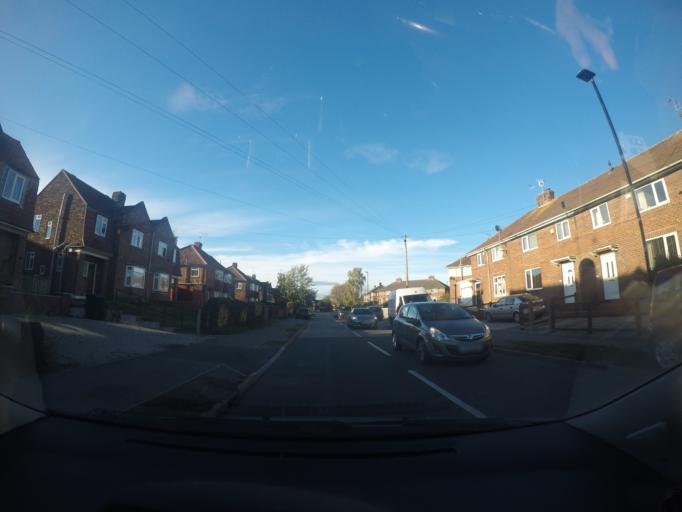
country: GB
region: England
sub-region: City of York
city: York
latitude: 53.9719
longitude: -1.0955
